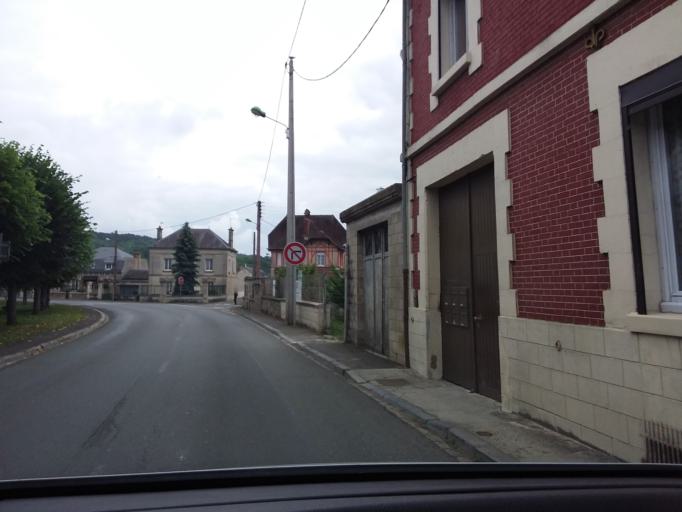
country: FR
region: Picardie
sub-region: Departement de l'Aisne
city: Vailly-sur-Aisne
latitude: 49.4082
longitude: 3.5169
